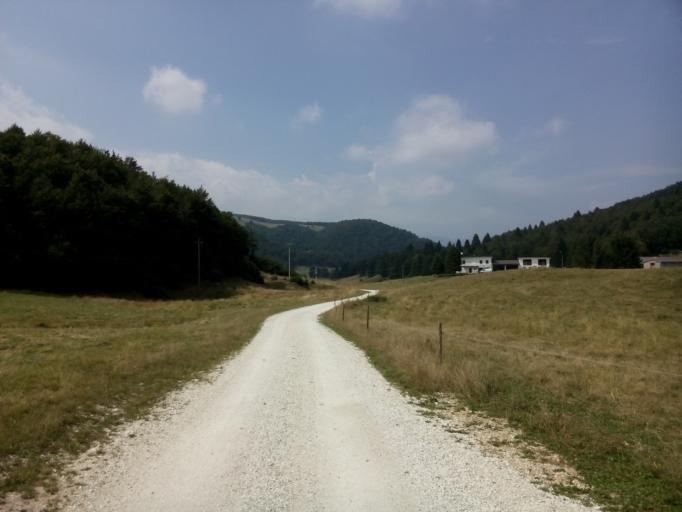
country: IT
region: Veneto
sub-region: Provincia di Vicenza
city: San Nazario
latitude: 45.8126
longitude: 11.6687
